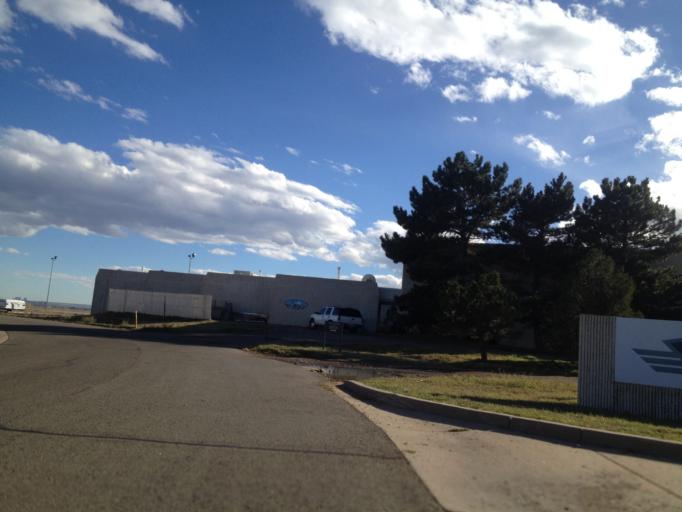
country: US
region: Colorado
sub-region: Broomfield County
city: Broomfield
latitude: 39.9131
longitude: -105.1169
